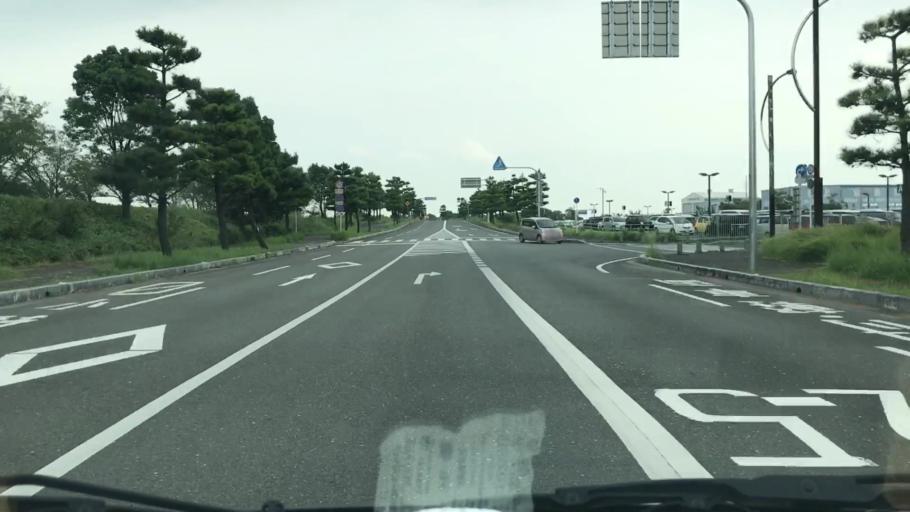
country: JP
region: Saga Prefecture
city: Okawa
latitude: 33.1542
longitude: 130.3044
